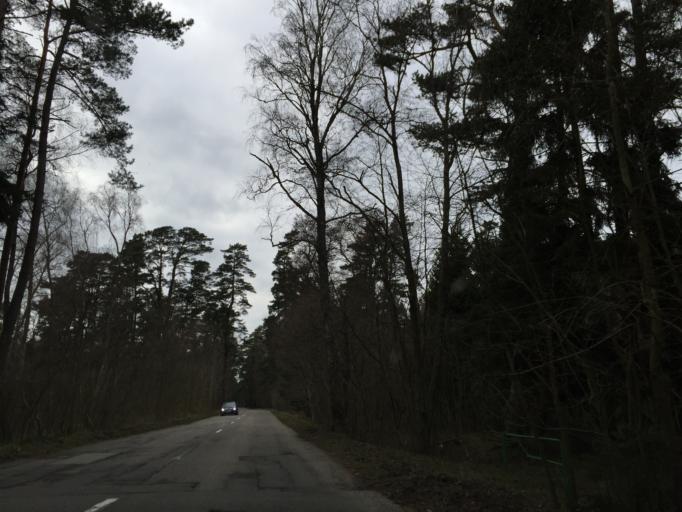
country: LT
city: Nida
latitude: 55.3206
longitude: 21.0032
